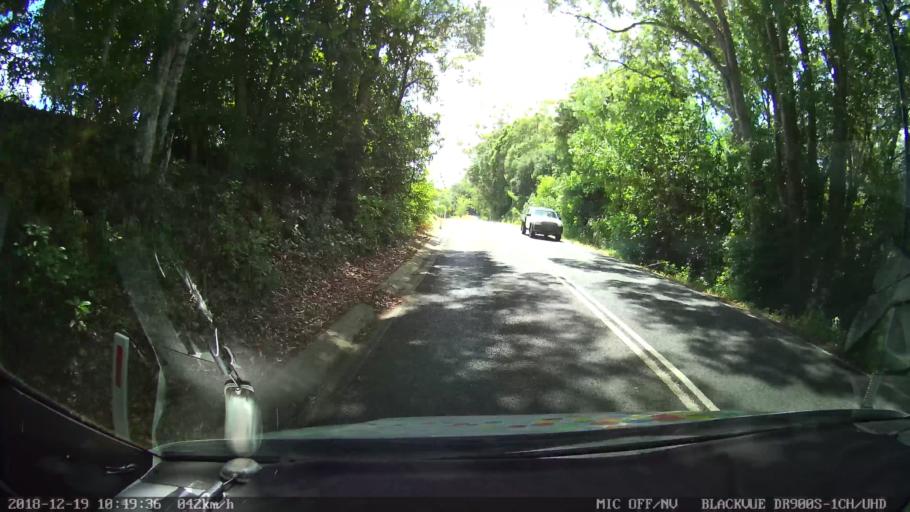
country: AU
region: New South Wales
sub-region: Lismore Municipality
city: Nimbin
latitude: -28.6012
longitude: 153.2198
